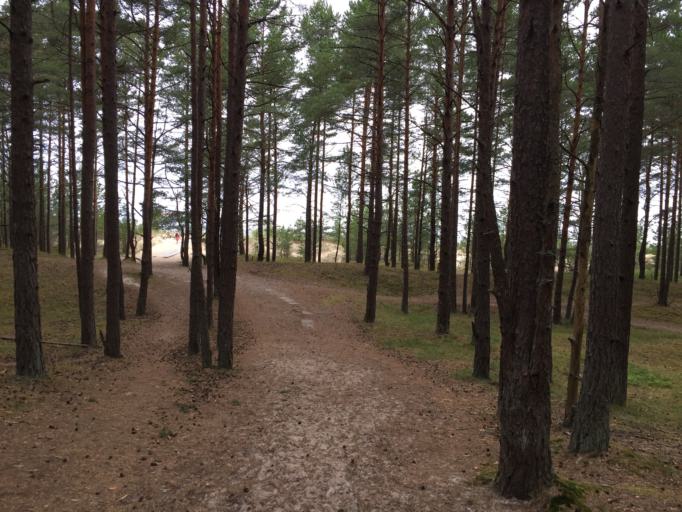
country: LV
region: Carnikava
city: Carnikava
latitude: 57.1245
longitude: 24.2136
